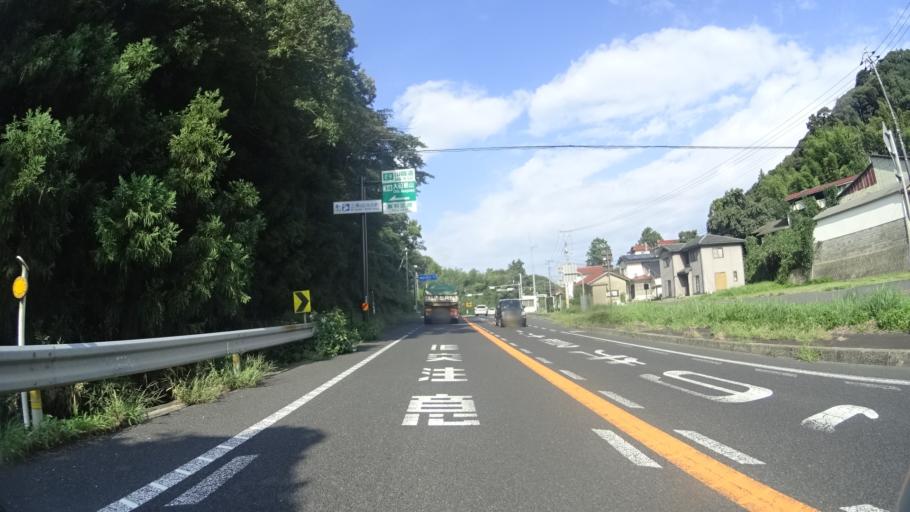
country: JP
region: Shimane
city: Odacho-oda
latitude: 35.2485
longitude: 132.5673
